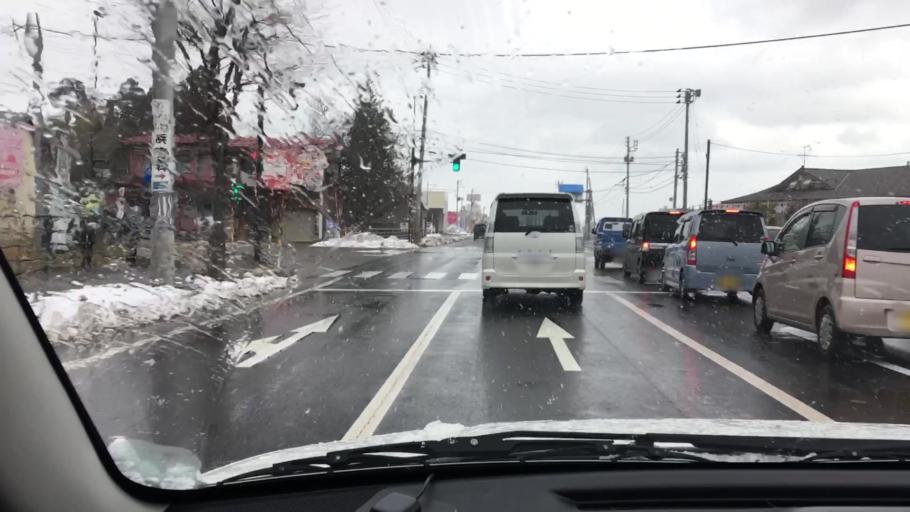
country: JP
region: Niigata
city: Joetsu
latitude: 37.1233
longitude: 138.2322
